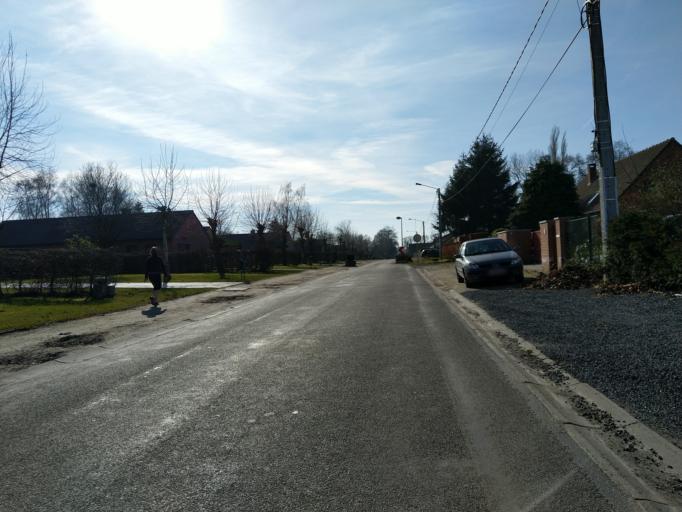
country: BE
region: Wallonia
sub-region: Province du Hainaut
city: Jurbise
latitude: 50.5140
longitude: 3.9598
